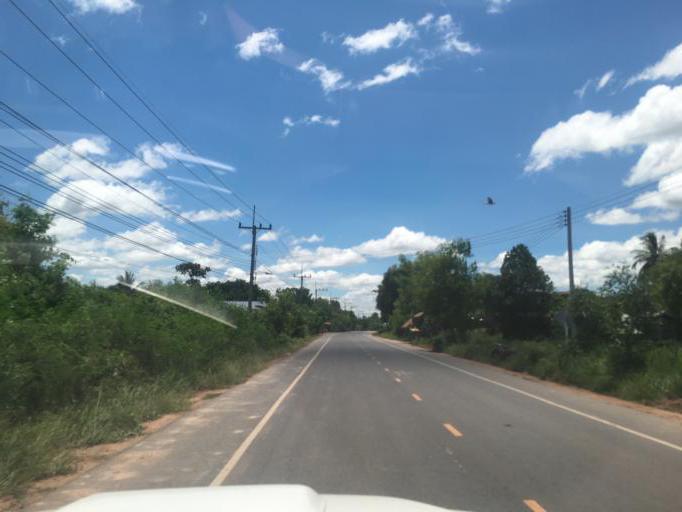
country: TH
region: Changwat Udon Thani
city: Nong Saeng
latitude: 17.2265
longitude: 102.7444
